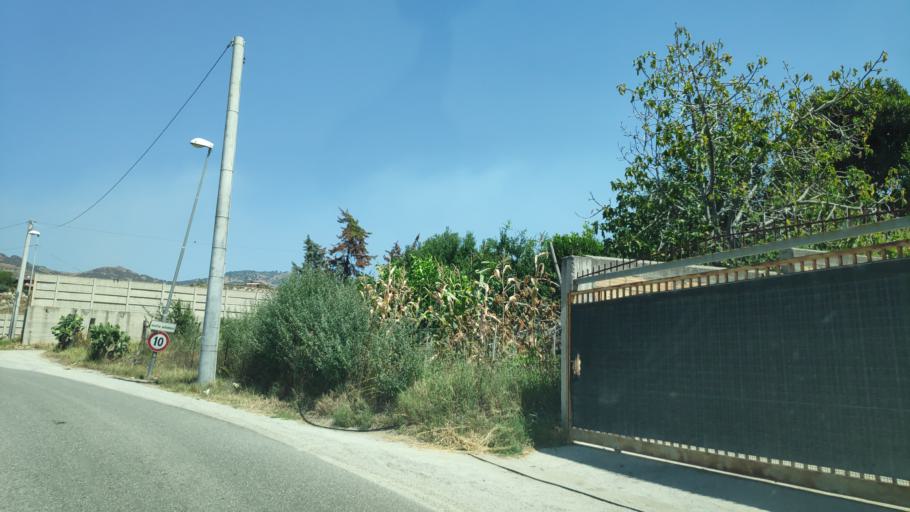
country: IT
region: Calabria
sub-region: Provincia di Reggio Calabria
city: Bova Marina
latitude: 37.9345
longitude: 15.9118
